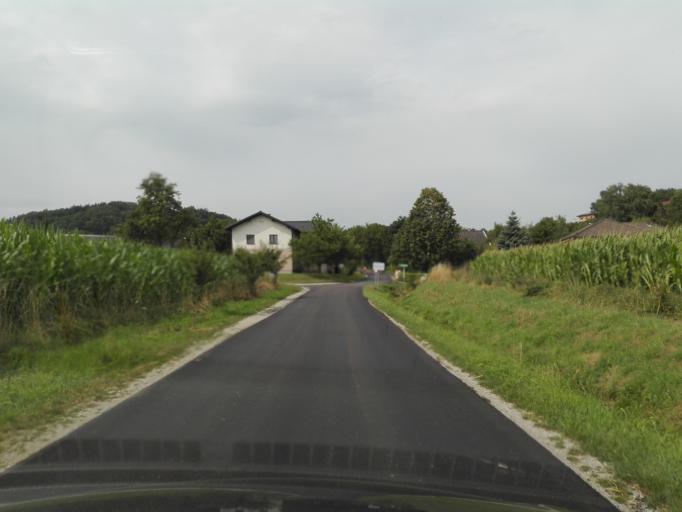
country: AT
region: Upper Austria
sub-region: Politischer Bezirk Perg
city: Perg
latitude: 48.2240
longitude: 14.7169
